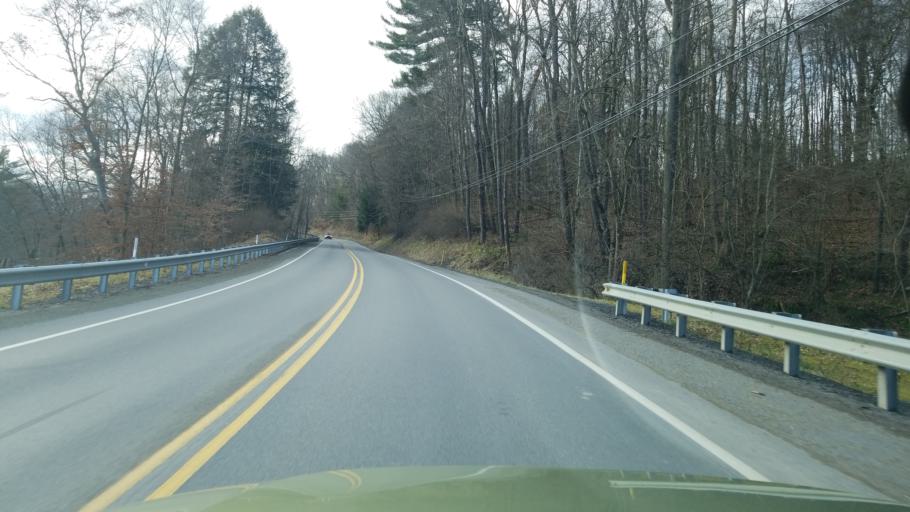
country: US
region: Pennsylvania
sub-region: Jefferson County
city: Albion
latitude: 40.9541
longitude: -78.9299
